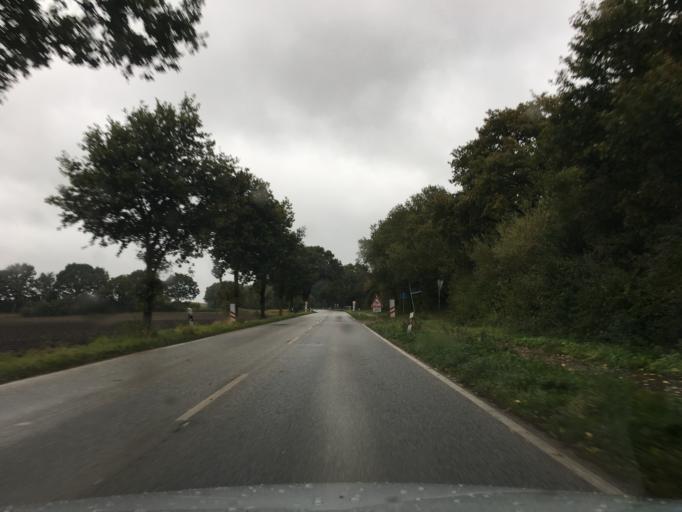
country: DE
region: Schleswig-Holstein
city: Ottendorf
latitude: 54.3793
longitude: 10.0581
